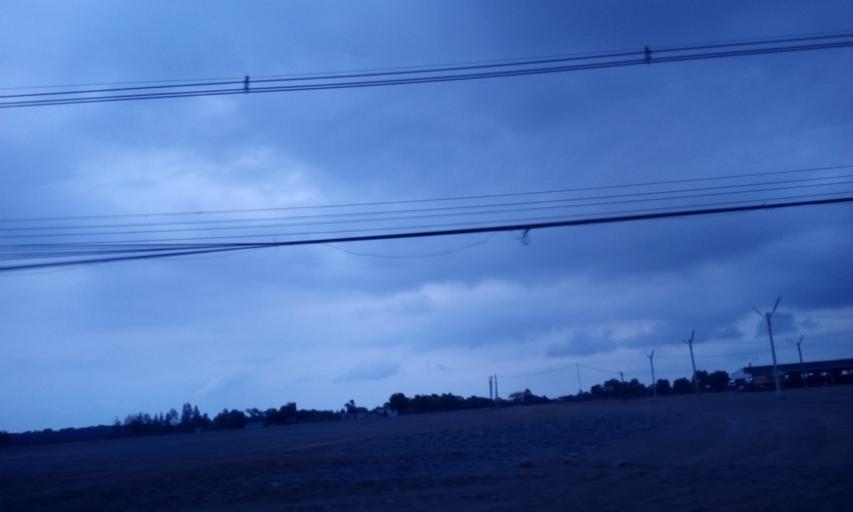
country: TH
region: Chanthaburi
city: Khlung
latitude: 12.4426
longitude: 102.2979
